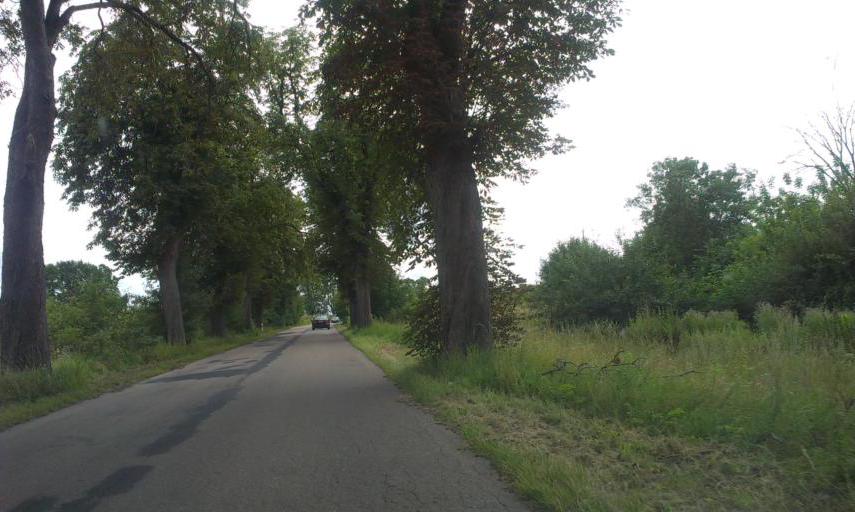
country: PL
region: West Pomeranian Voivodeship
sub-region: Powiat szczecinecki
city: Barwice
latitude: 53.7327
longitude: 16.3555
